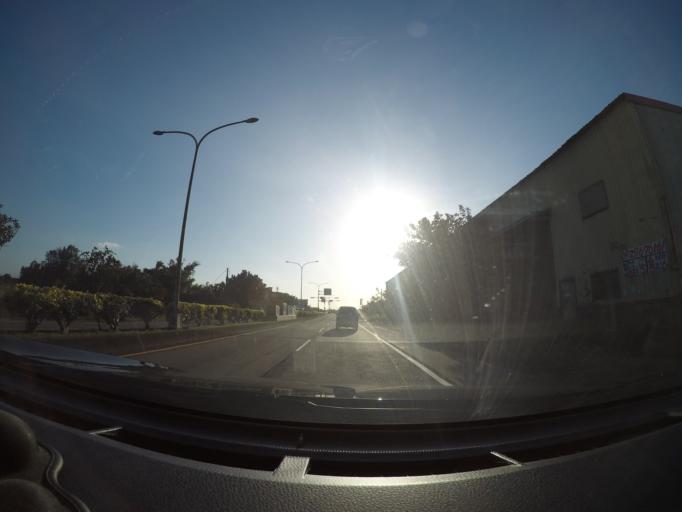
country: TW
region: Taiwan
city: Taoyuan City
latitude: 25.0767
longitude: 121.2051
